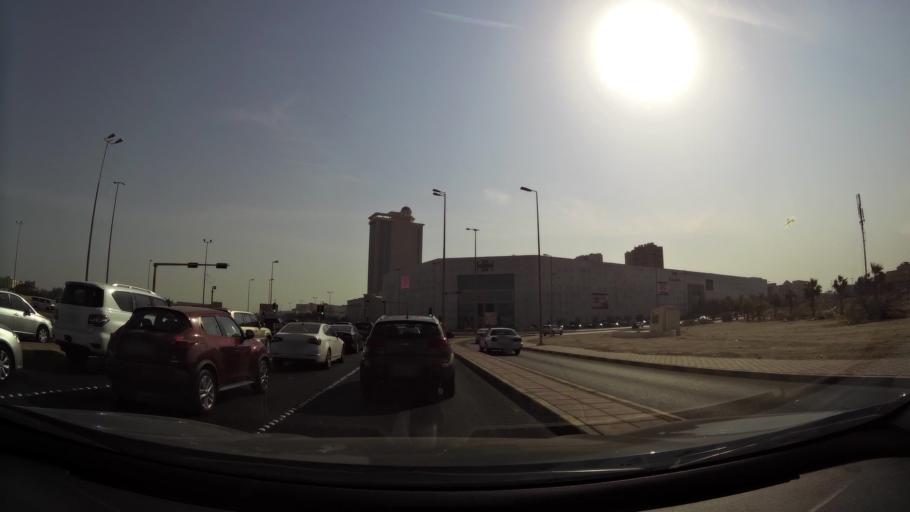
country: KW
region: Mubarak al Kabir
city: Mubarak al Kabir
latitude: 29.1766
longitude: 48.0998
